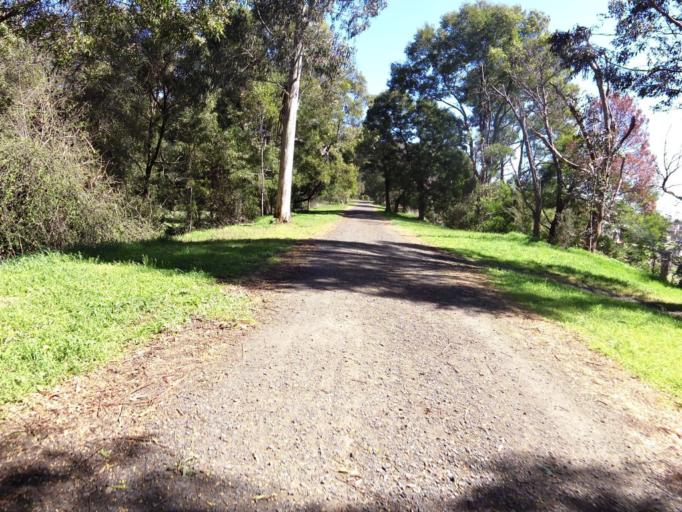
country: AU
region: Victoria
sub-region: Latrobe
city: Moe
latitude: -38.1764
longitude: 146.2710
